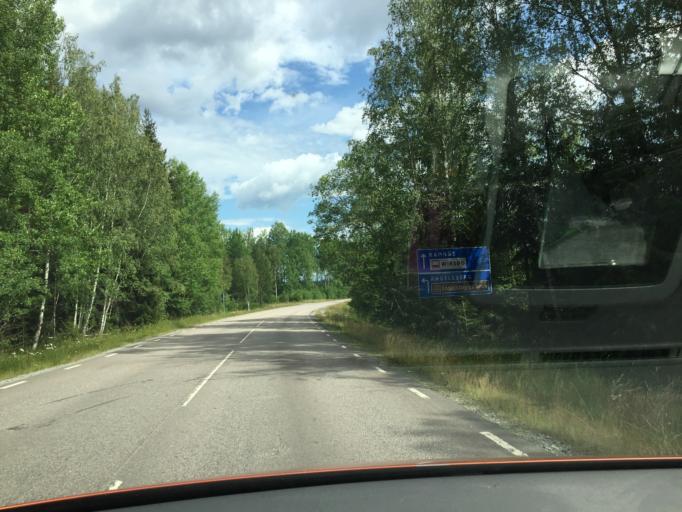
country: SE
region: Vaestmanland
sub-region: Surahammars Kommun
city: Ramnas
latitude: 59.8824
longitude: 16.0653
